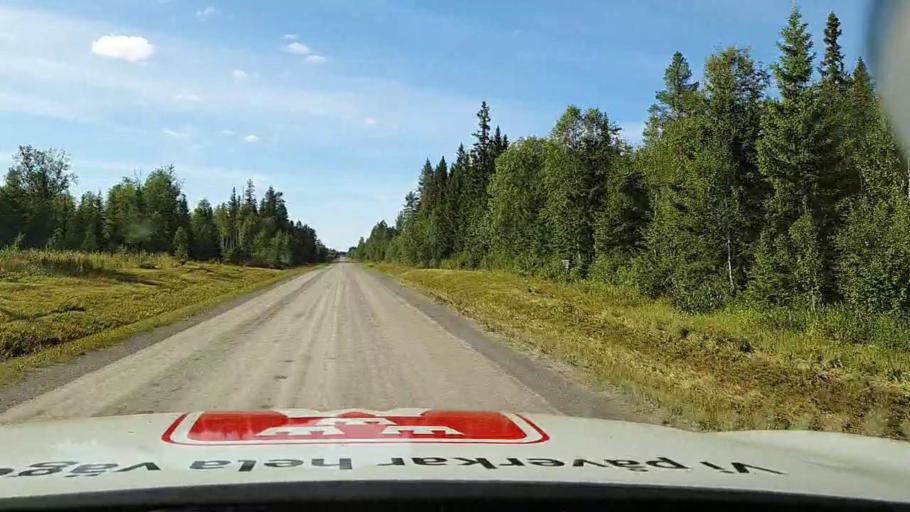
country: SE
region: Jaemtland
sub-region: OEstersunds Kommun
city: Lit
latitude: 63.6709
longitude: 14.8856
